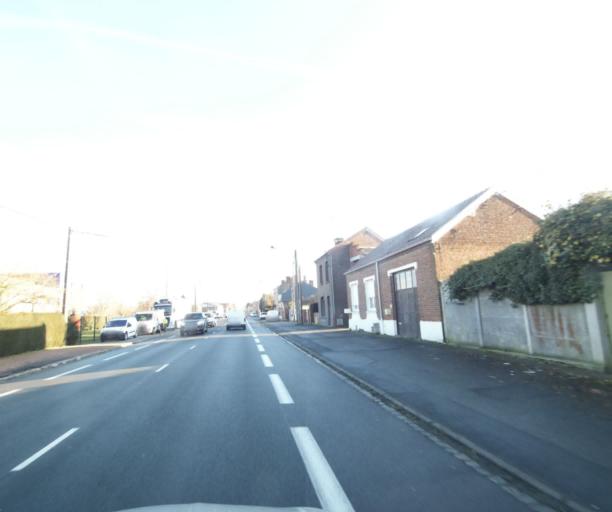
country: FR
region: Nord-Pas-de-Calais
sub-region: Departement du Nord
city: Marly
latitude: 50.3438
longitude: 3.5593
